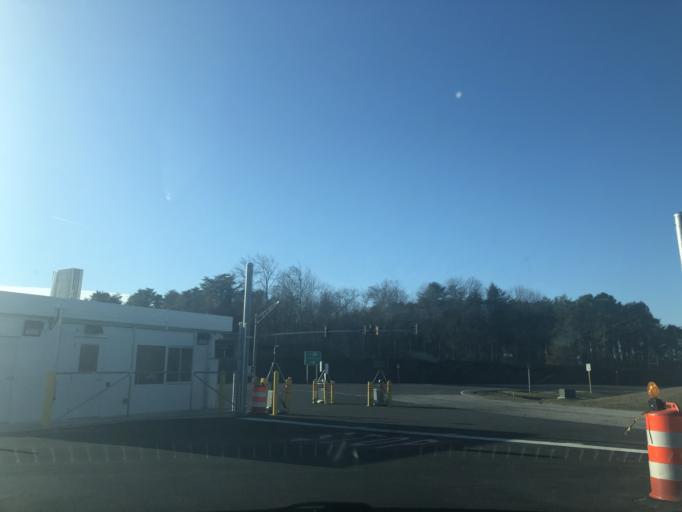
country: US
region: Maryland
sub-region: Anne Arundel County
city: Severn
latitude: 39.1712
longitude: -76.6886
